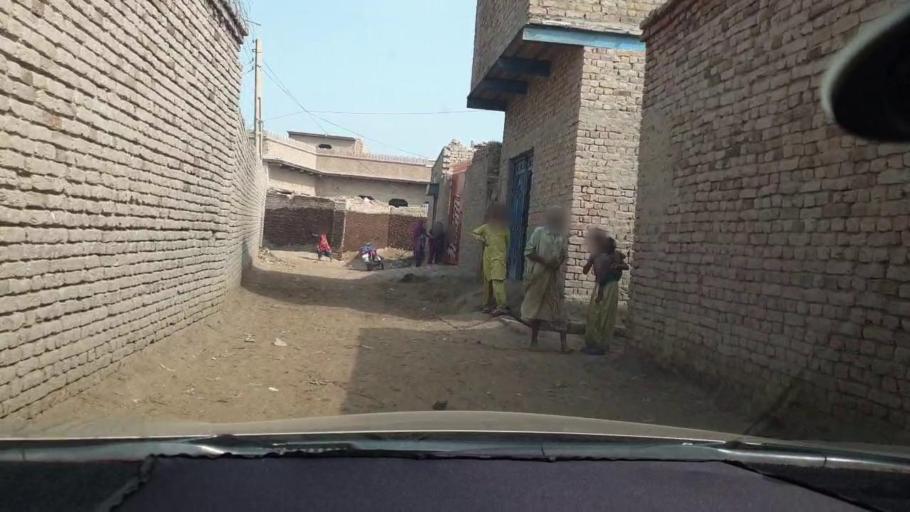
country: PK
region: Sindh
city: Kambar
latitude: 27.5430
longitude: 68.0465
